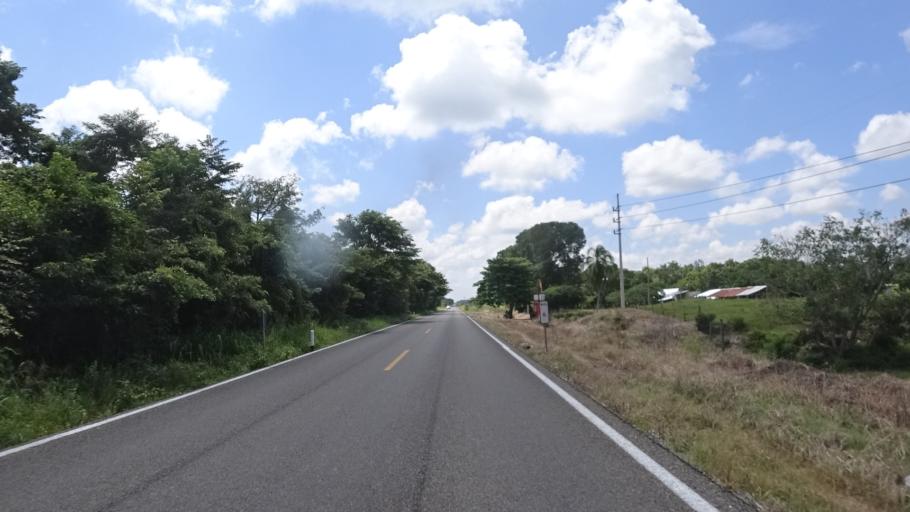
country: MX
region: Campeche
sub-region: Carmen
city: Licenciado Gustavo Diaz Ordaz (18 de Marzo)
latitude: 18.6833
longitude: -90.9767
